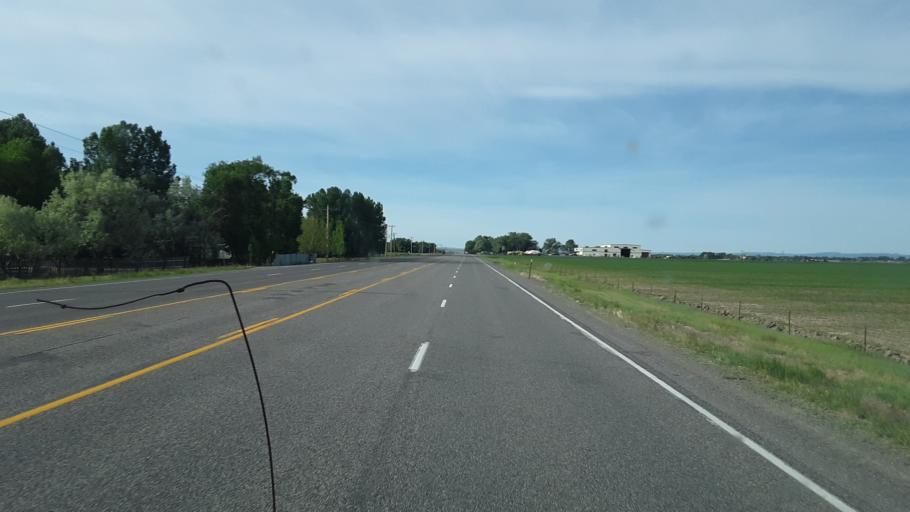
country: US
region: Wyoming
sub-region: Fremont County
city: Riverton
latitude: 43.0730
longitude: -108.3810
